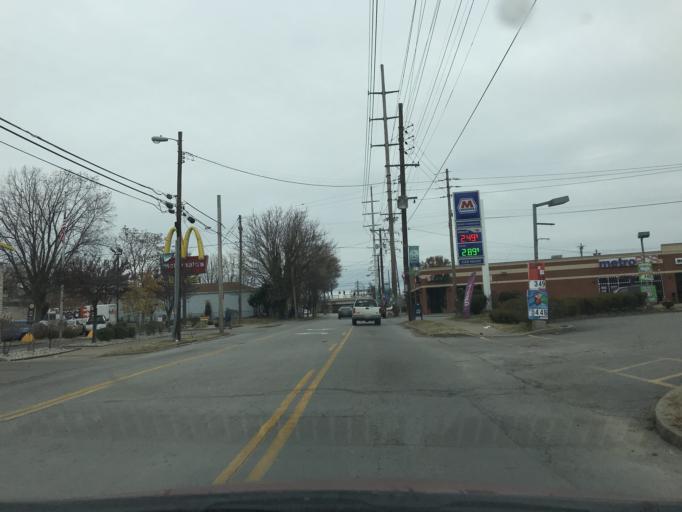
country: US
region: Kentucky
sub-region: Jefferson County
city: Louisville
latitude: 38.2670
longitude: -85.7833
